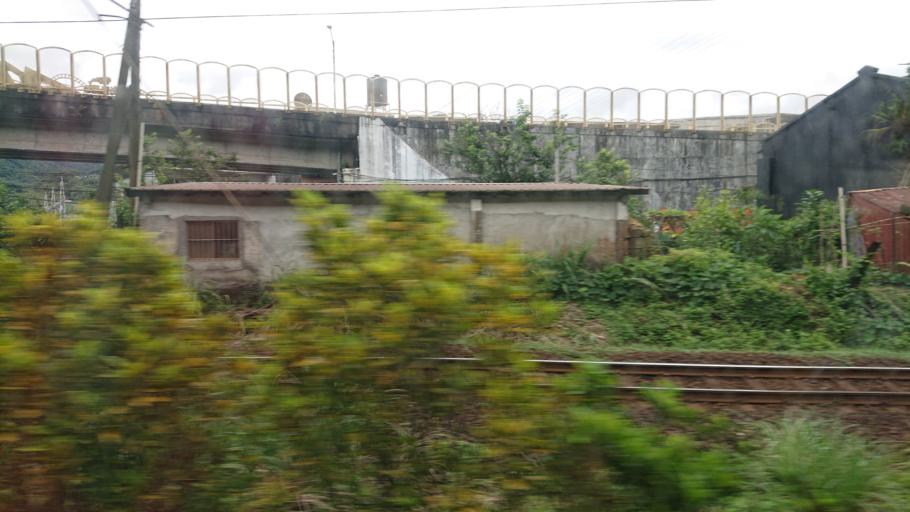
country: TW
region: Taiwan
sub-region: Keelung
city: Keelung
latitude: 25.1071
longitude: 121.8206
